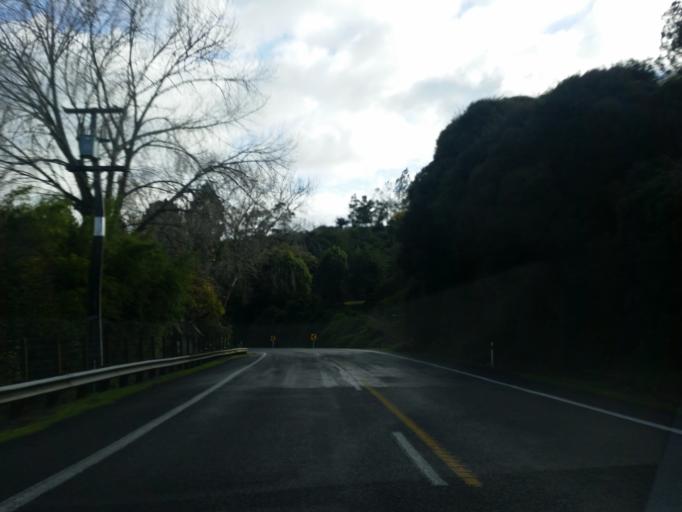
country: NZ
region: Waikato
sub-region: Hauraki District
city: Waihi
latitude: -37.4121
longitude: 175.7780
